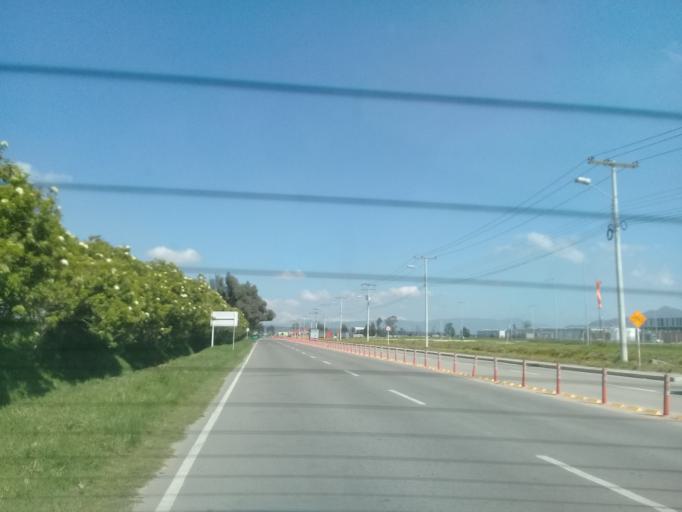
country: CO
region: Cundinamarca
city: Funza
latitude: 4.7324
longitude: -74.1603
